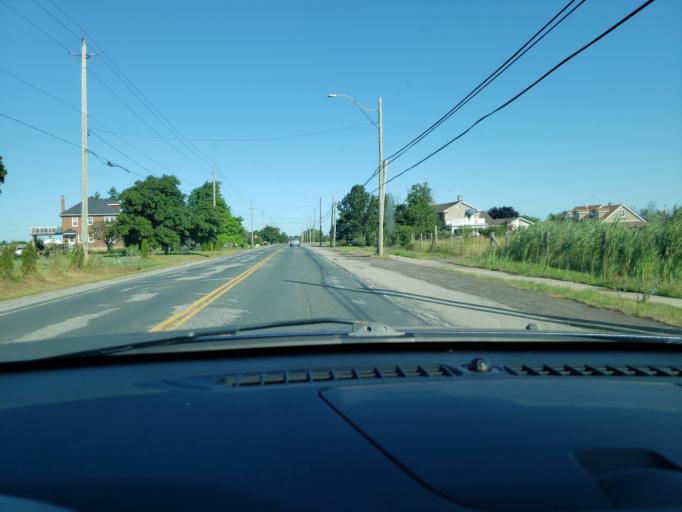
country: CA
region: Ontario
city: Hamilton
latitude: 43.2011
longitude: -79.6101
